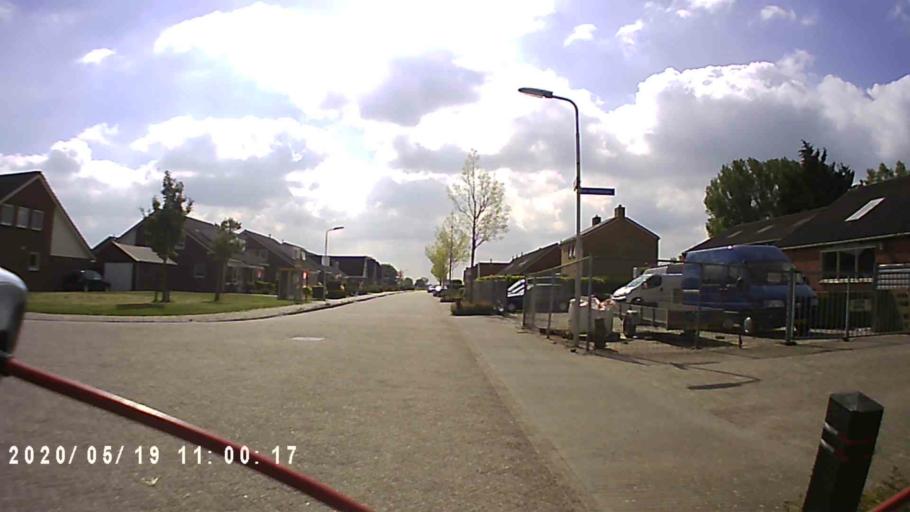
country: NL
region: Groningen
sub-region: Gemeente Zuidhorn
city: Grijpskerk
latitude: 53.3044
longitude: 6.2680
